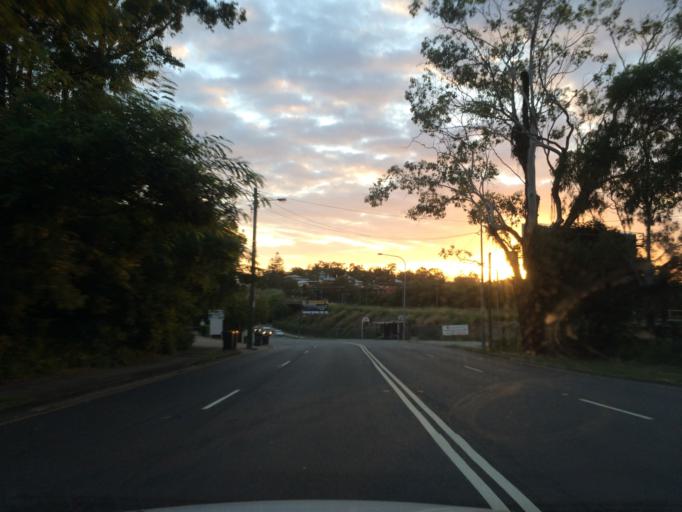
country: AU
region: Queensland
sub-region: Brisbane
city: Taringa
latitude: -27.4909
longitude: 152.9848
